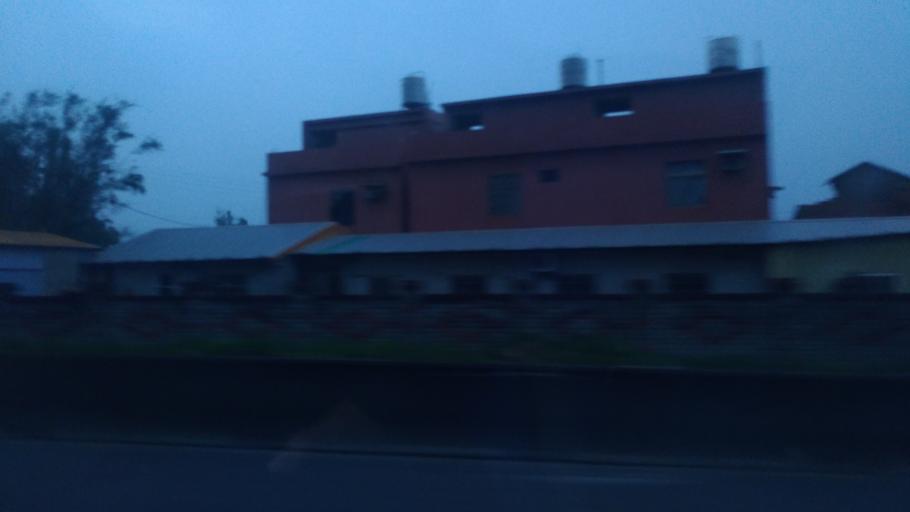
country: TW
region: Taiwan
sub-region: Miaoli
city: Miaoli
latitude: 24.5793
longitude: 120.7204
